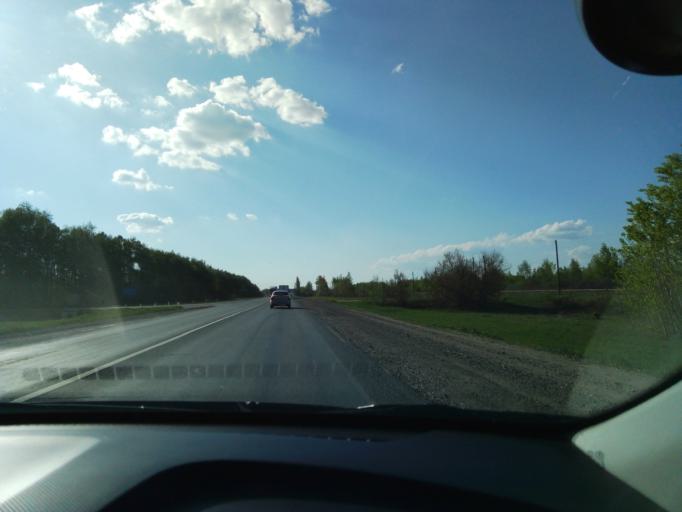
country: RU
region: Chuvashia
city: Kugesi
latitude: 56.0560
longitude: 47.2686
